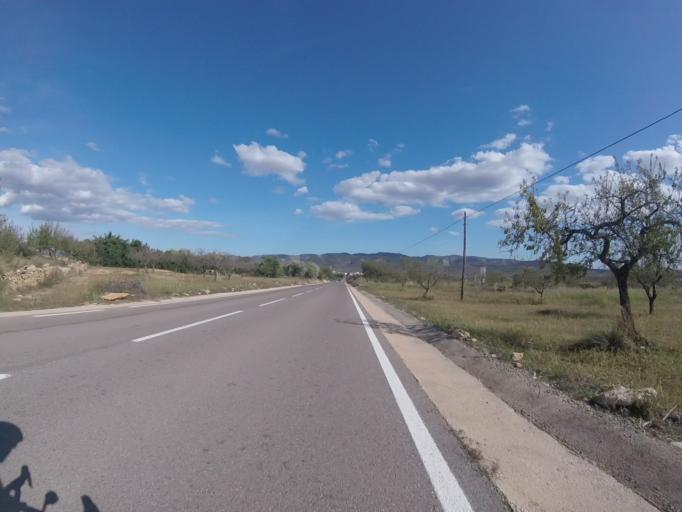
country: ES
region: Valencia
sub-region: Provincia de Castello
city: Alcala de Xivert
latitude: 40.3024
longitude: 0.2004
